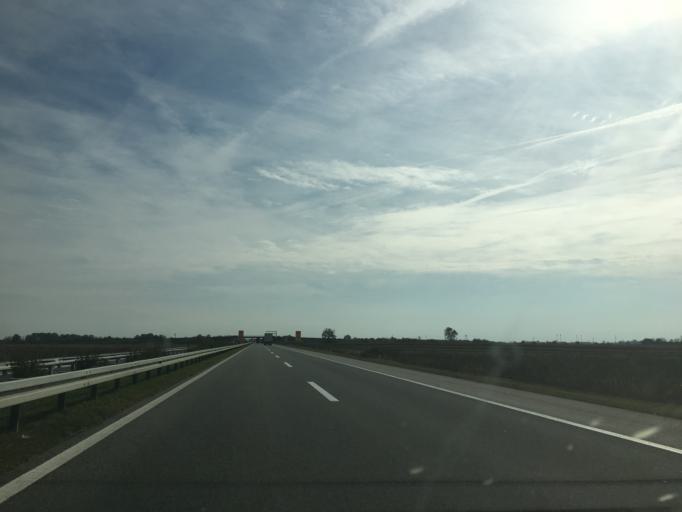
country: RS
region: Autonomna Pokrajina Vojvodina
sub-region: Sremski Okrug
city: Stara Pazova
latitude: 45.0162
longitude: 20.1958
